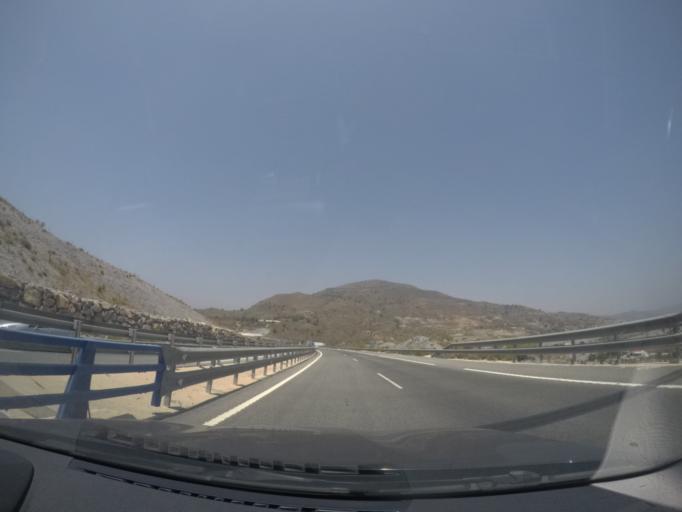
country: ES
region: Andalusia
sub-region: Provincia de Granada
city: Motril
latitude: 36.7858
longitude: -3.5094
